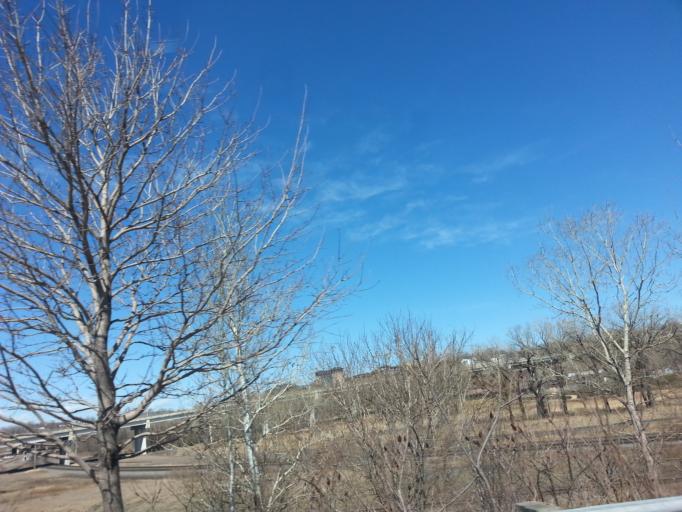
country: US
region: Minnesota
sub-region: Ramsey County
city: Saint Paul
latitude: 44.9496
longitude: -93.0751
